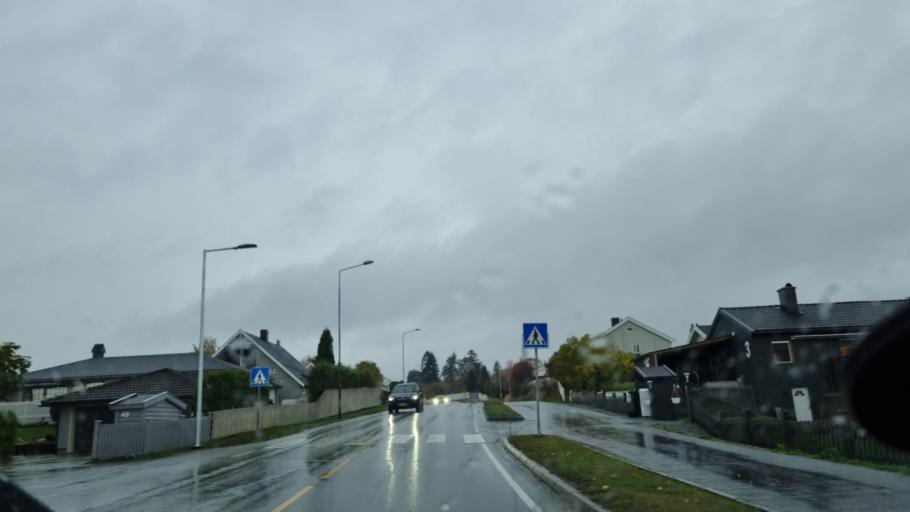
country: NO
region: Hedmark
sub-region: Hamar
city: Hamar
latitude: 60.8034
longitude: 11.1292
